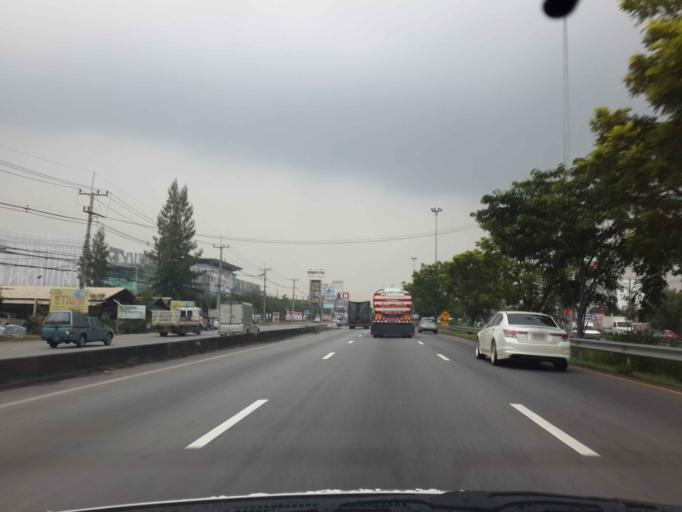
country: TH
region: Bangkok
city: Bang Bon
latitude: 13.6090
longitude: 100.3768
